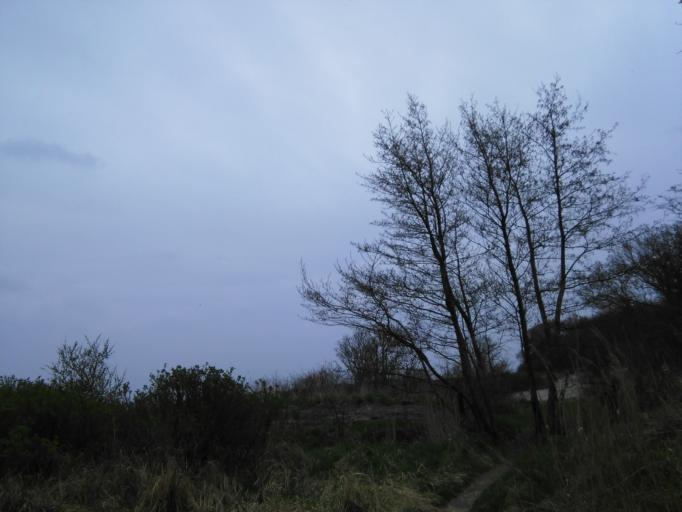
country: DK
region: Central Jutland
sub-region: Arhus Kommune
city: Beder
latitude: 56.0546
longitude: 10.2643
